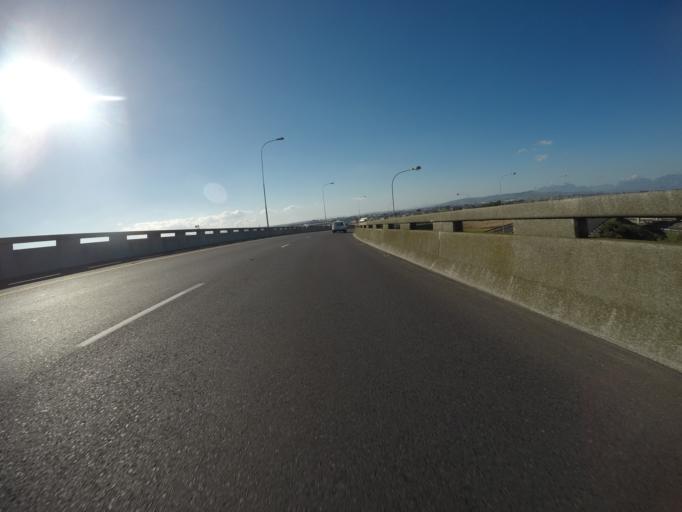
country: ZA
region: Western Cape
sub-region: City of Cape Town
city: Lansdowne
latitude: -33.9999
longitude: 18.6330
